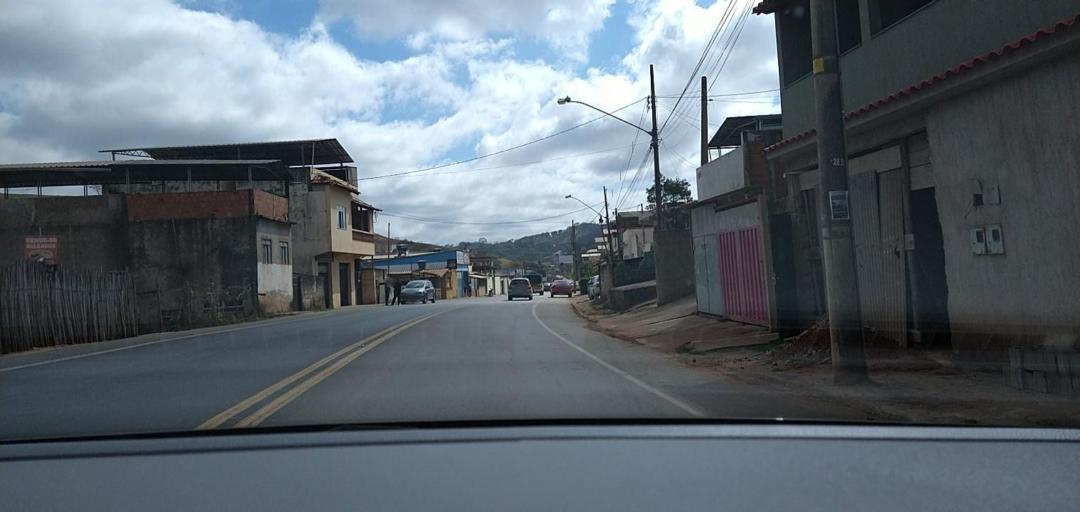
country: BR
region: Minas Gerais
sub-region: Vicosa
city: Vicosa
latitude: -20.6634
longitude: -42.8565
